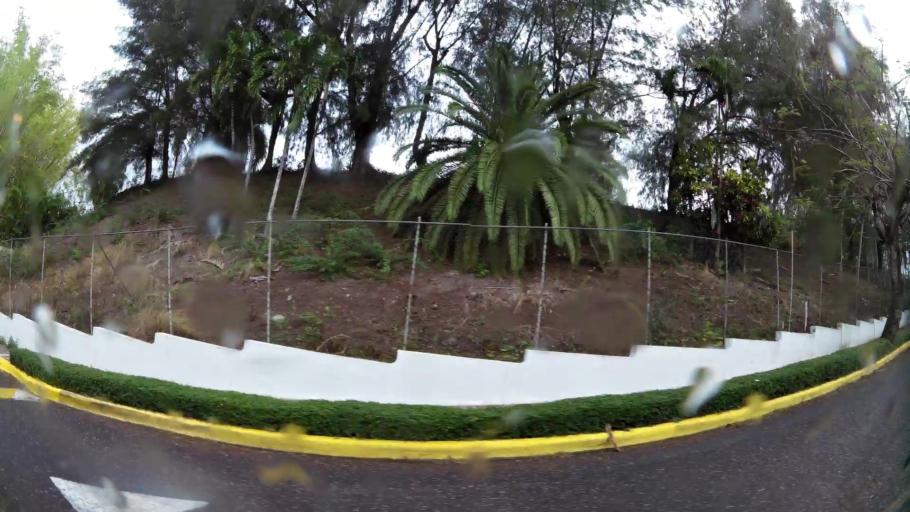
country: DO
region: Nacional
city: La Agustina
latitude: 18.5120
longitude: -69.9366
